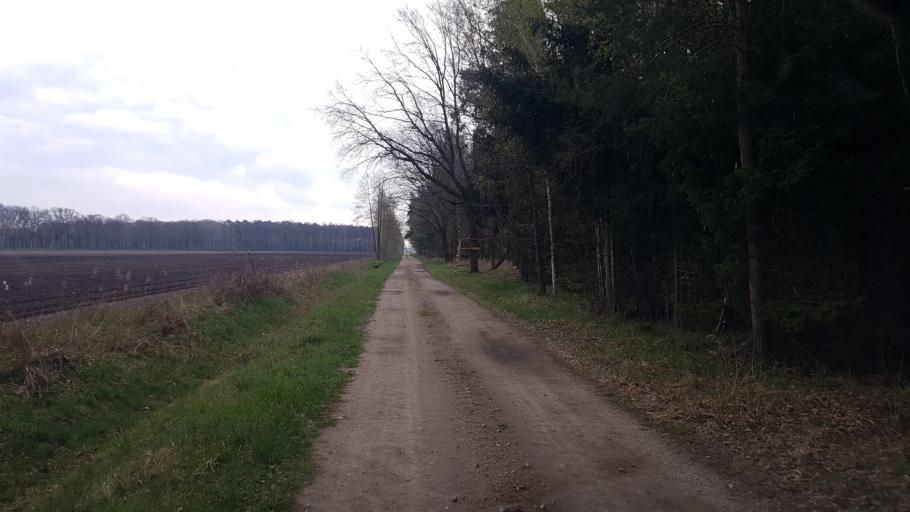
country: DE
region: Brandenburg
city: Bronkow
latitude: 51.6265
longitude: 13.8961
